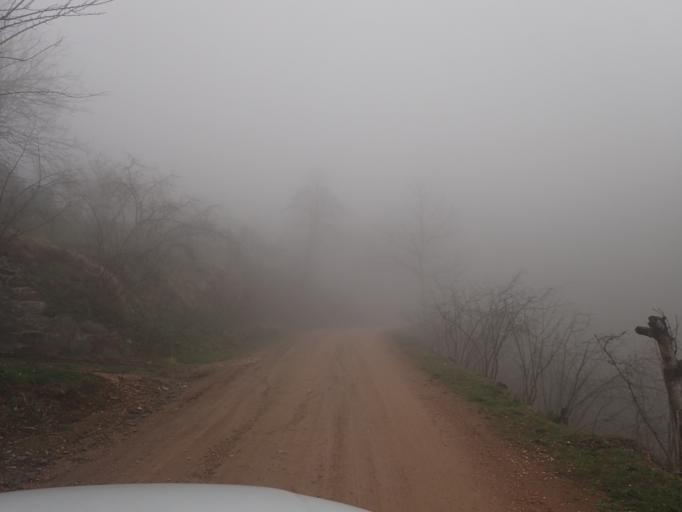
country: TR
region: Ordu
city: Camas
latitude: 40.9041
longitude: 37.5638
